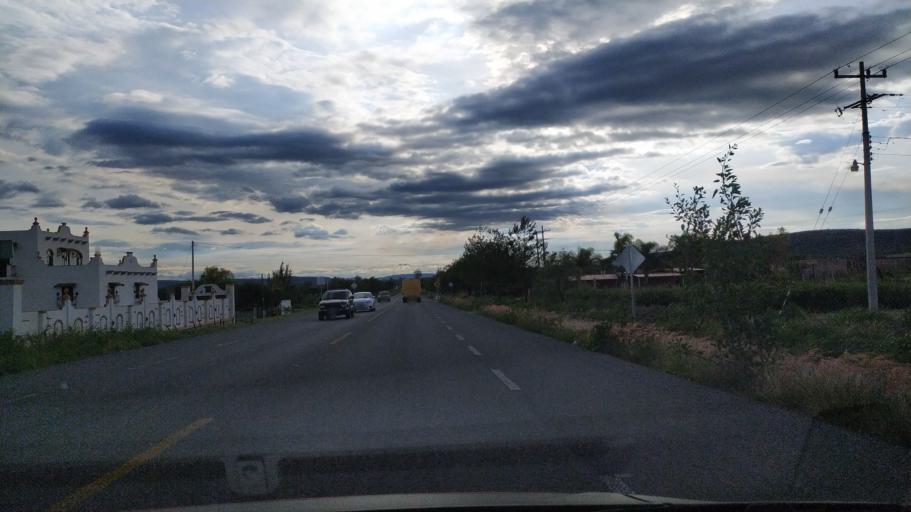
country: MX
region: Guanajuato
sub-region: San Francisco del Rincon
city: San Ignacio de Hidalgo
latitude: 20.8915
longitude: -101.9481
